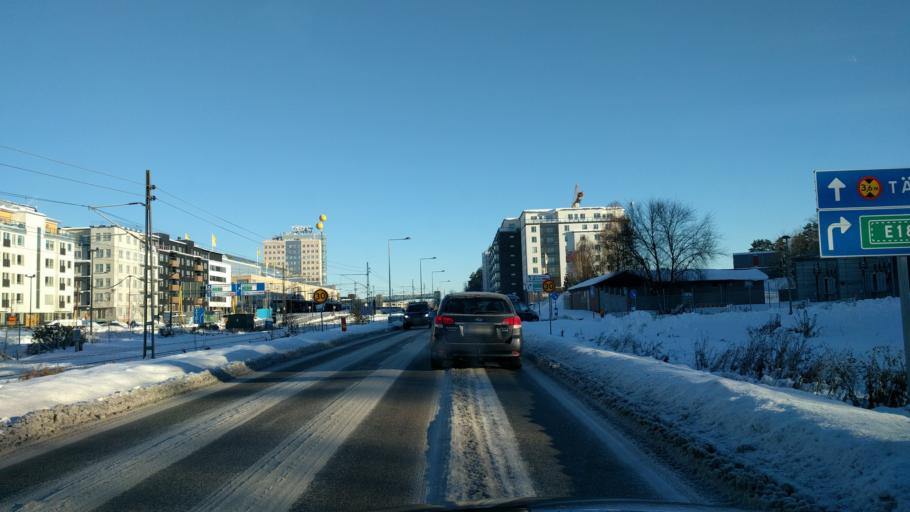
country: SE
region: Stockholm
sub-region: Taby Kommun
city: Taby
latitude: 59.4414
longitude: 18.0688
